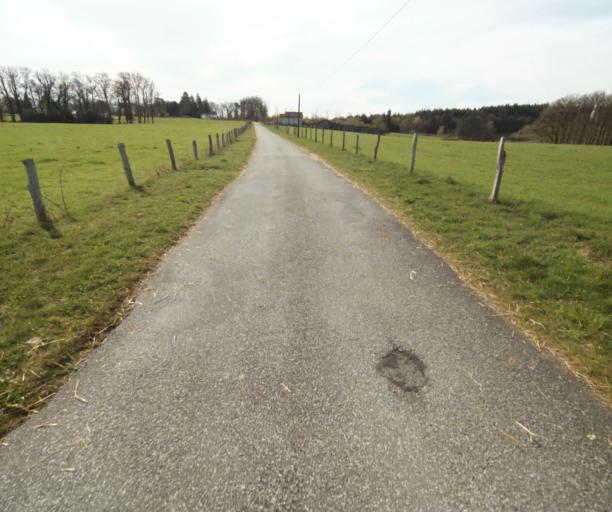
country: FR
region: Limousin
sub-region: Departement de la Correze
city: Correze
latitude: 45.3355
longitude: 1.8677
